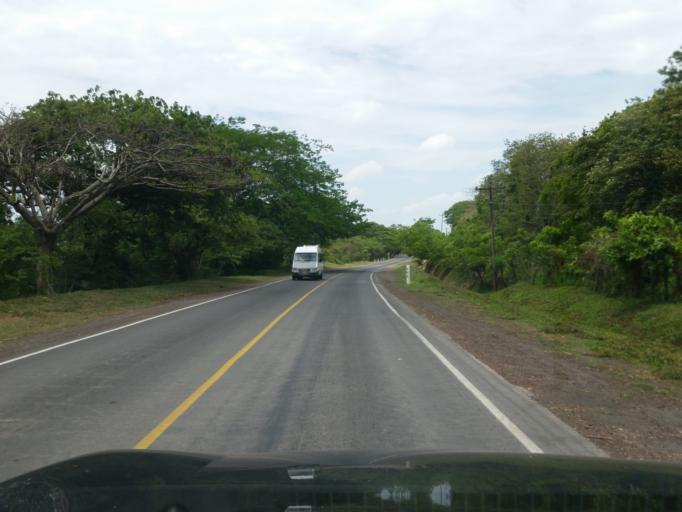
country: NI
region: Granada
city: Nandaime
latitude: 11.8044
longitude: -86.0447
